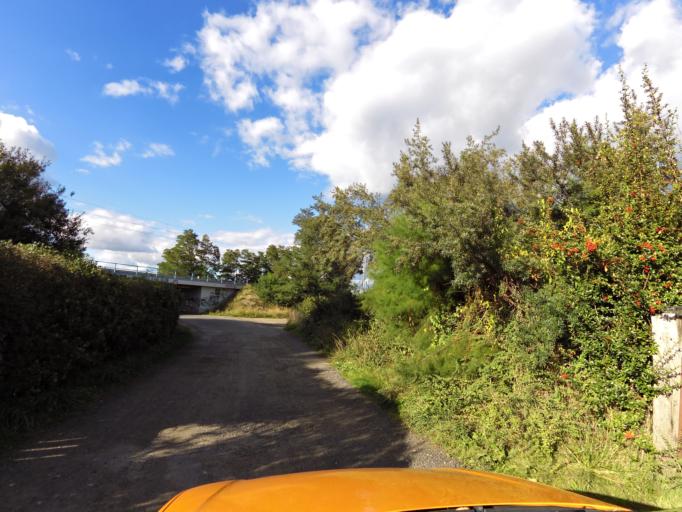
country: DE
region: Brandenburg
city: Luckenwalde
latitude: 52.0988
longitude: 13.1710
